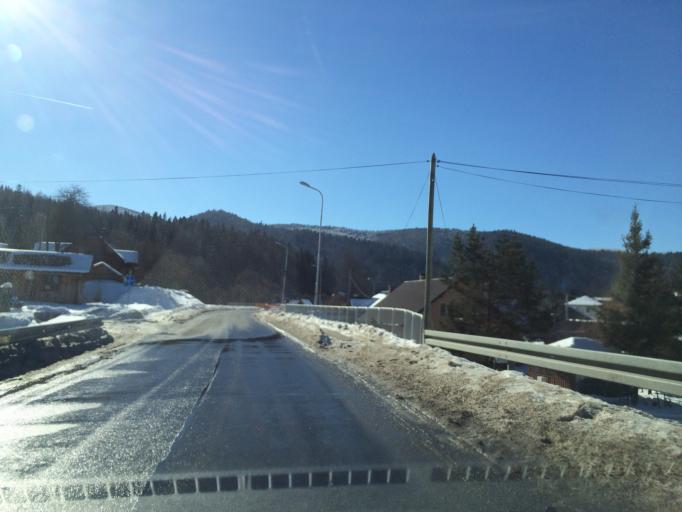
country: PL
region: Subcarpathian Voivodeship
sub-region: Powiat leski
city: Cisna
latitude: 49.2144
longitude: 22.3340
